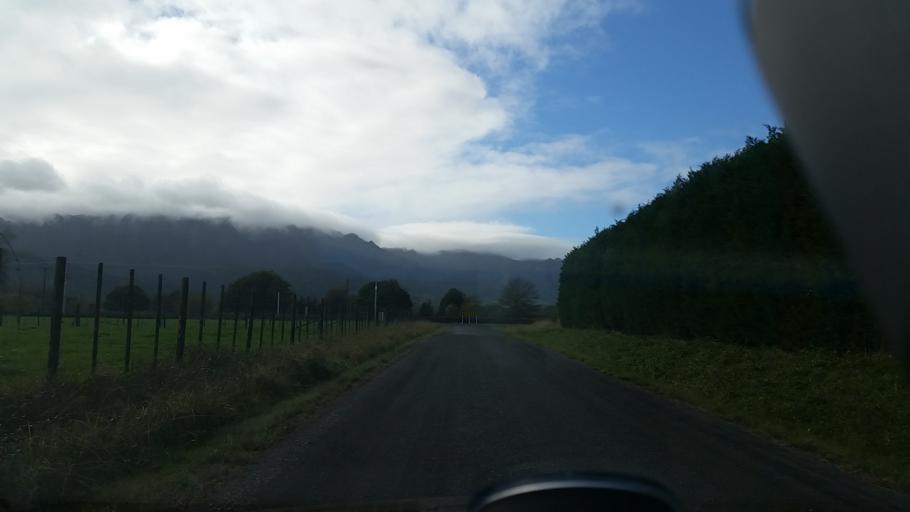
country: NZ
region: Bay of Plenty
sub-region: Western Bay of Plenty District
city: Katikati
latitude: -37.5774
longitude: 175.7312
